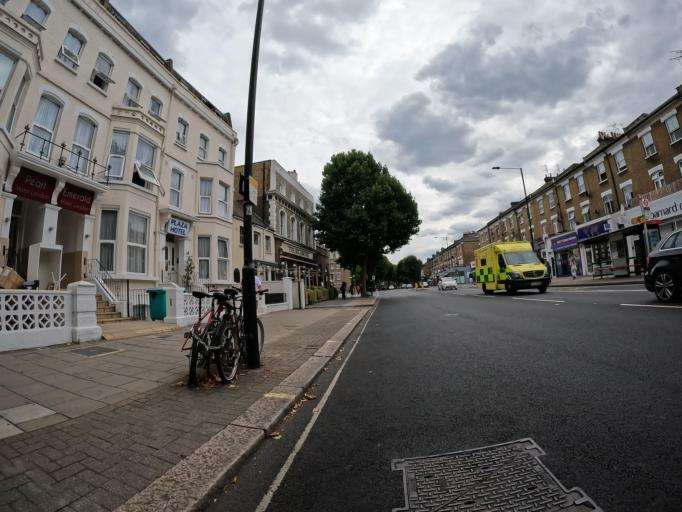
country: GB
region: England
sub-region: Greater London
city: Hammersmith
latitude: 51.5006
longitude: -0.2218
